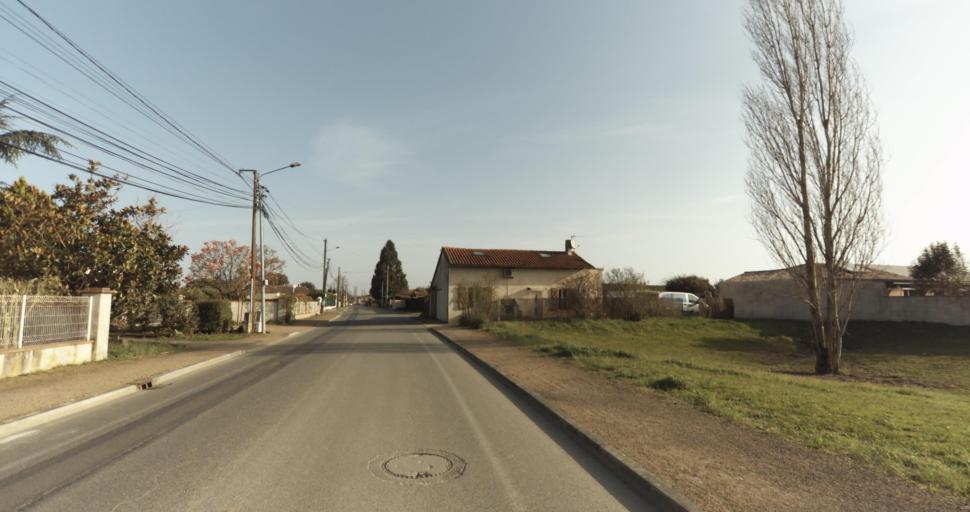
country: FR
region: Midi-Pyrenees
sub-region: Departement du Tarn
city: Saint-Sulpice-la-Pointe
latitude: 43.7643
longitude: 1.6877
